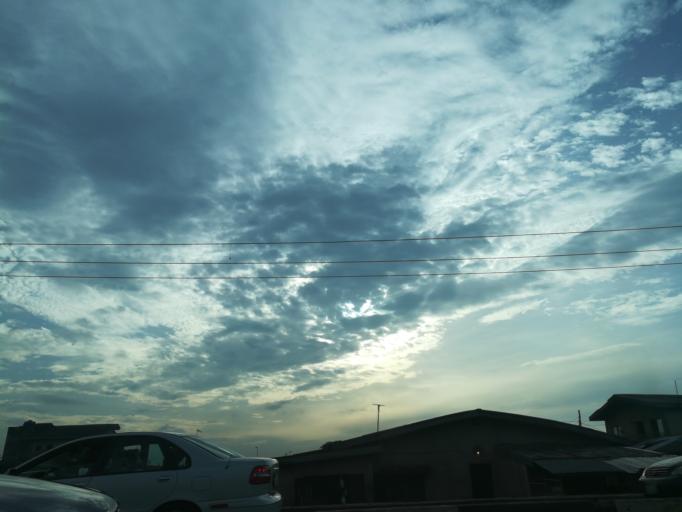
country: NG
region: Lagos
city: Ebute Ikorodu
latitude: 6.6162
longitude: 3.4755
